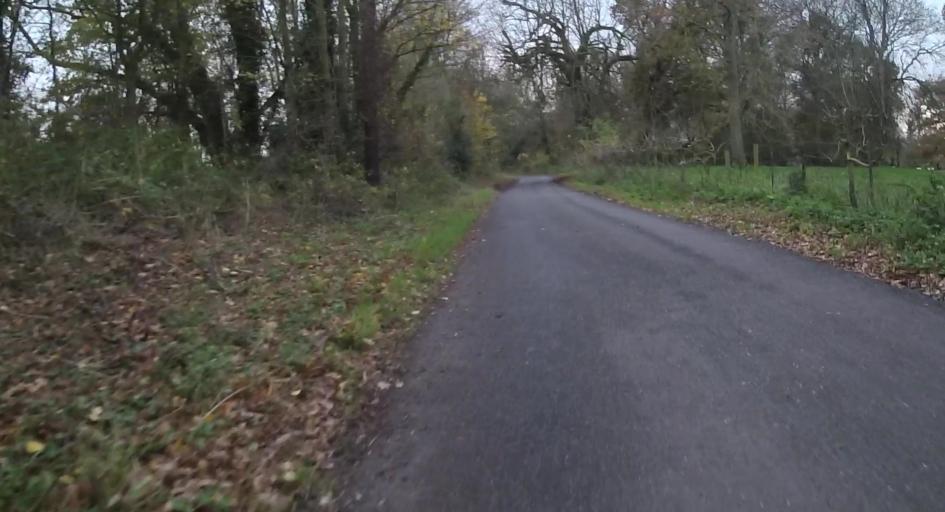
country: GB
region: England
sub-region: Hampshire
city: Long Sutton
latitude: 51.2172
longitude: -0.9643
